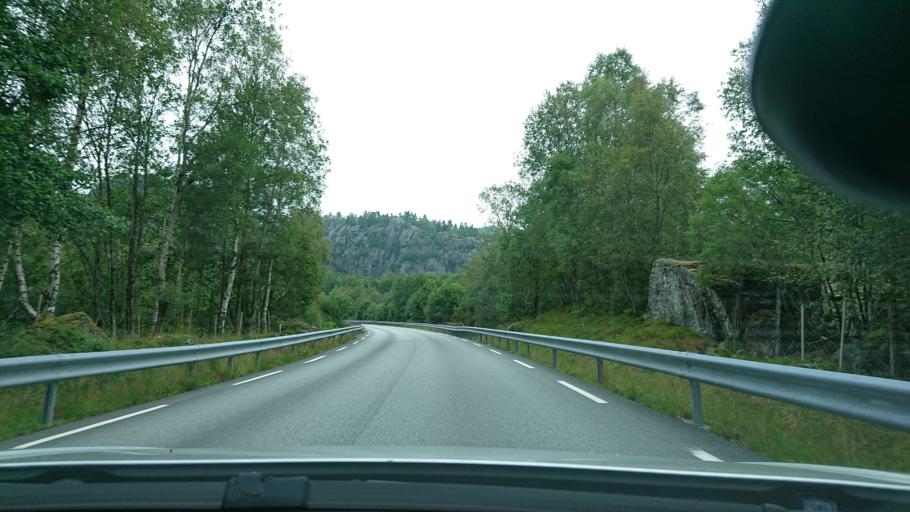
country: NO
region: Rogaland
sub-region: Hjelmeland
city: Hjelmelandsvagen
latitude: 59.2184
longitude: 6.2268
